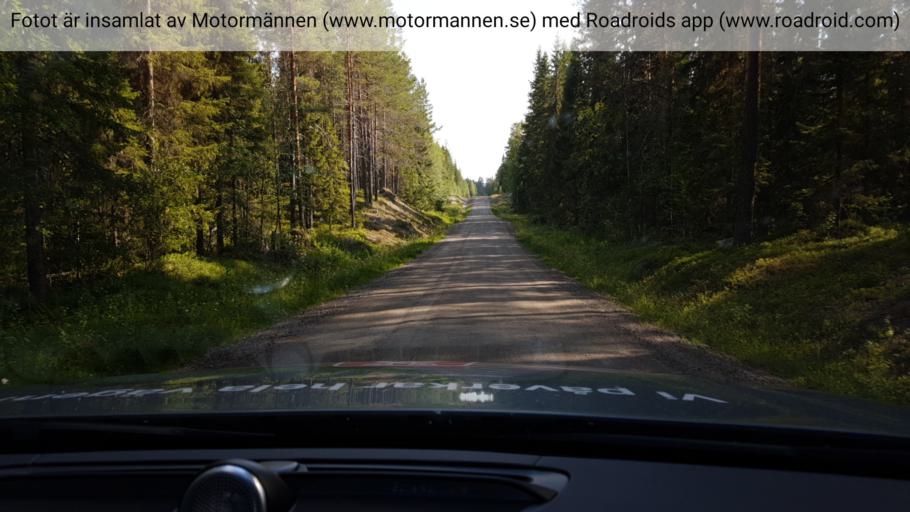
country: SE
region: Vaesterbotten
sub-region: Dorotea Kommun
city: Dorotea
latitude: 63.9515
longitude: 16.0763
